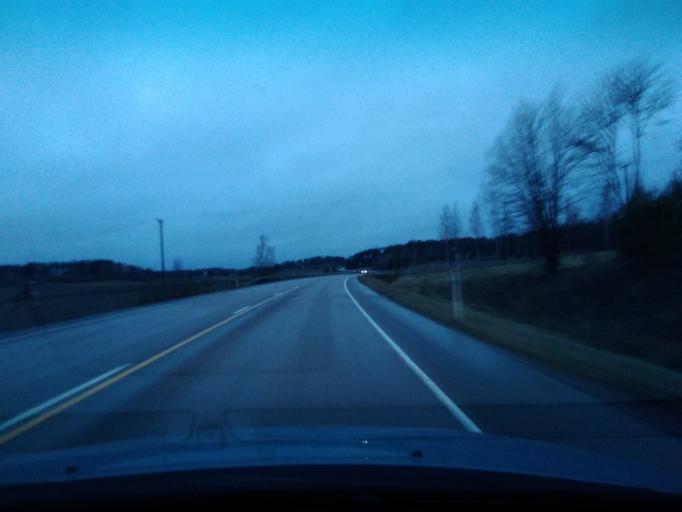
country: FI
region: Uusimaa
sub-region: Porvoo
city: Askola
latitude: 60.4784
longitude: 25.5656
